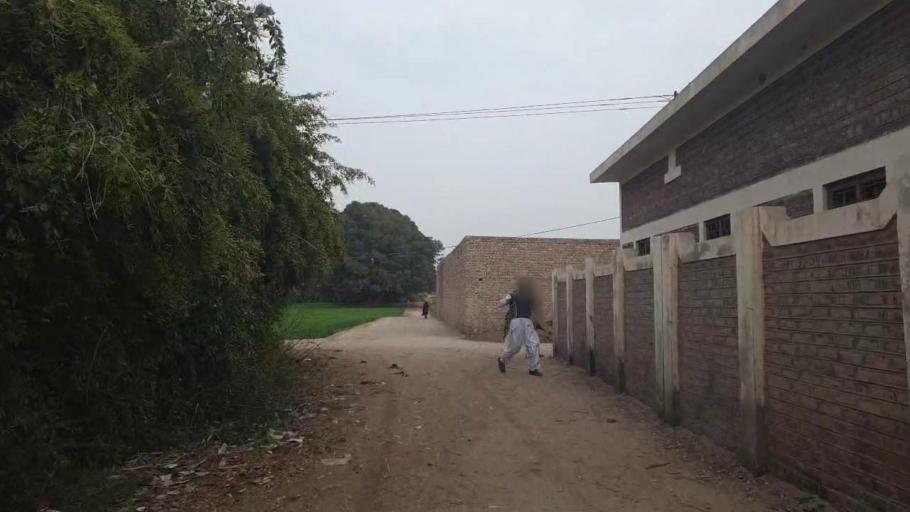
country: PK
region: Sindh
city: Tando Adam
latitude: 25.7883
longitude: 68.6552
